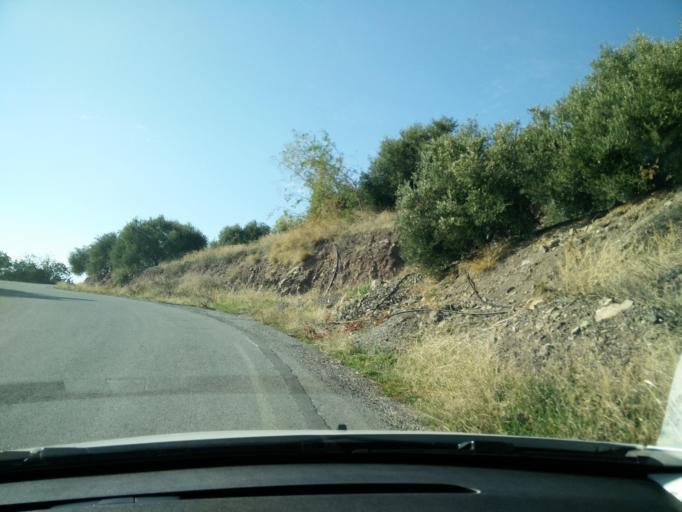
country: GR
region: Crete
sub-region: Nomos Lasithiou
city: Gra Liyia
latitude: 34.9955
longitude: 25.5203
